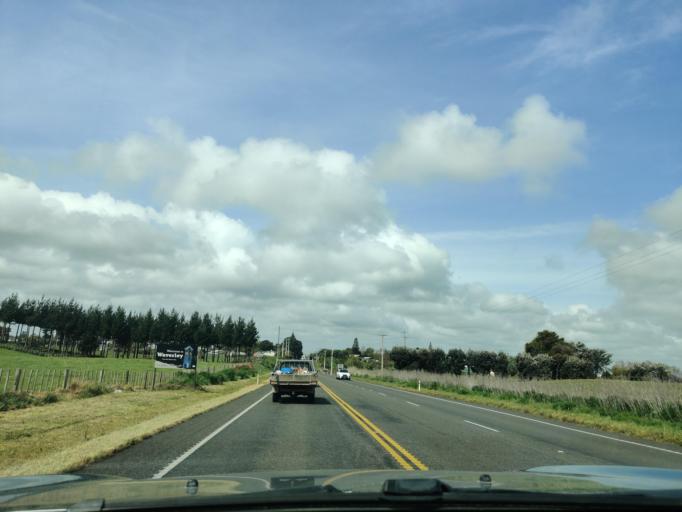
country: NZ
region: Taranaki
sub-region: South Taranaki District
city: Patea
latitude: -39.7652
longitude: 174.6199
